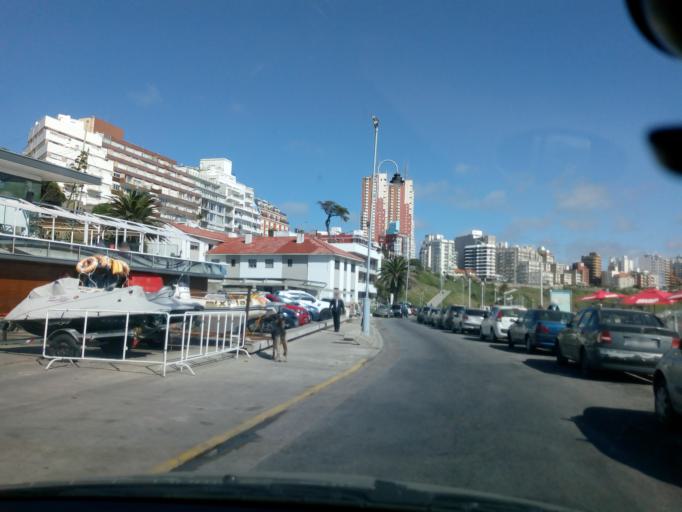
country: AR
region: Buenos Aires
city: Mar del Plata
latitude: -38.0164
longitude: -57.5252
